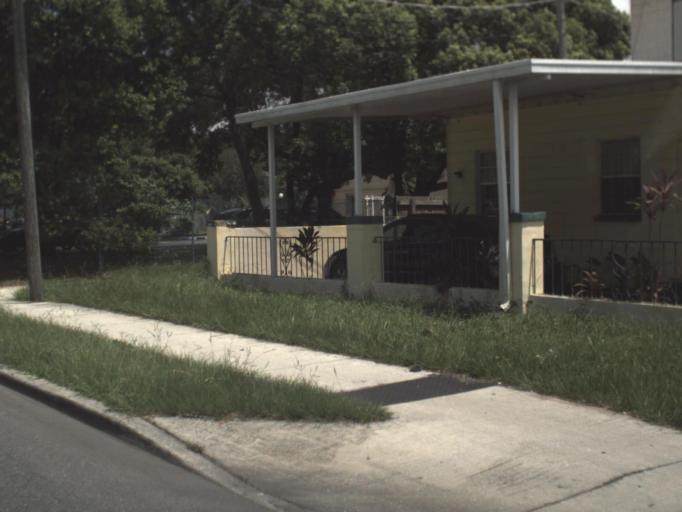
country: US
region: Florida
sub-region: Hillsborough County
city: Tampa
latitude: 27.9753
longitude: -82.4512
